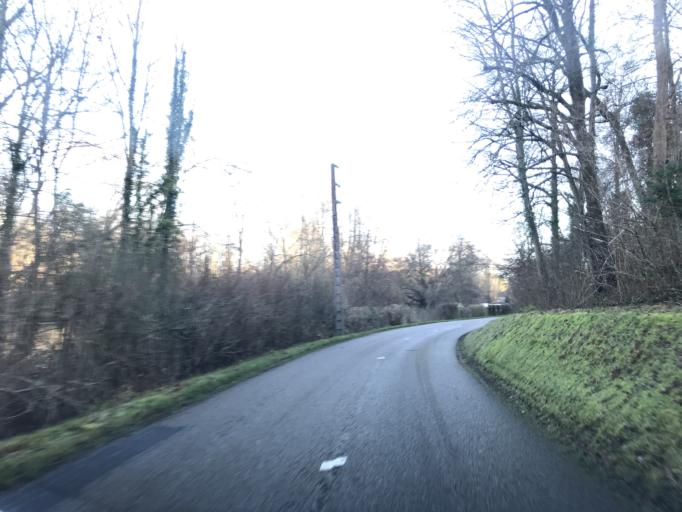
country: FR
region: Haute-Normandie
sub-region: Departement de l'Eure
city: Saint-Aubin-sur-Gaillon
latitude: 49.0911
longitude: 1.2614
